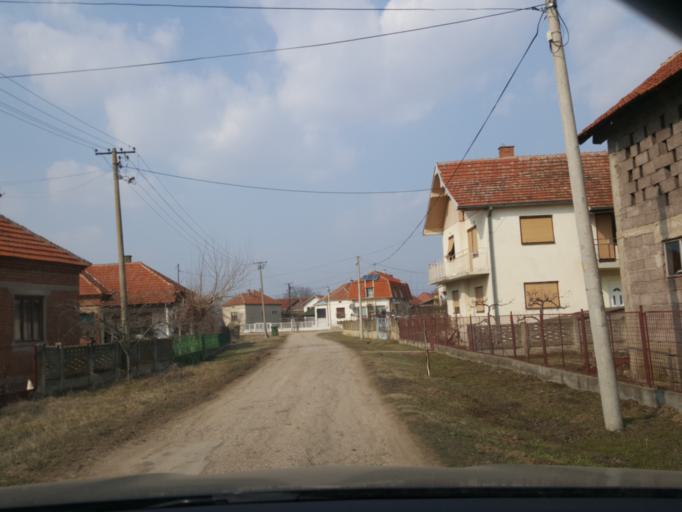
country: RS
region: Central Serbia
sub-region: Nisavski Okrug
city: Aleksinac
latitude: 43.4496
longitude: 21.7867
